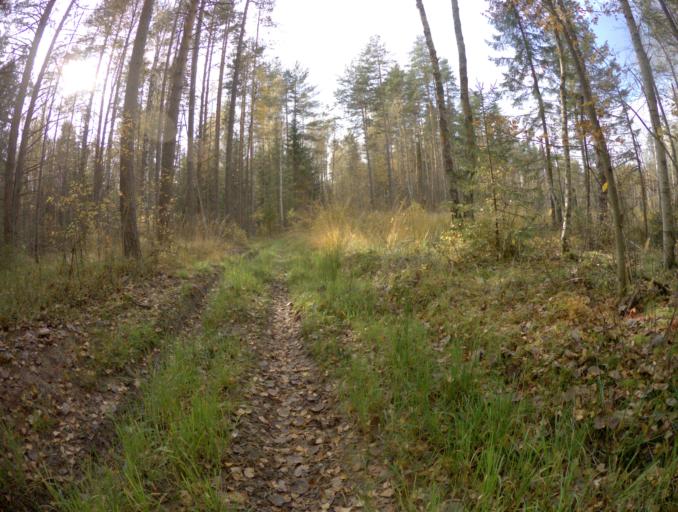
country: RU
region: Vladimir
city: Raduzhnyy
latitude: 55.9580
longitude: 40.3489
